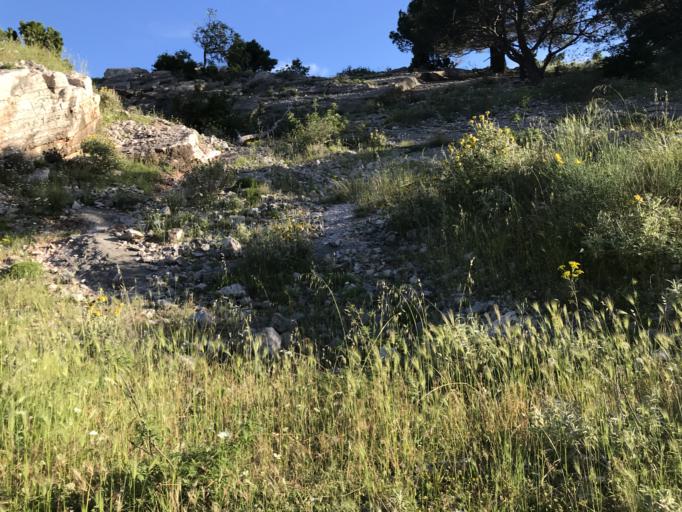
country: ME
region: Bar
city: Sutomore
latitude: 42.1374
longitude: 19.0474
